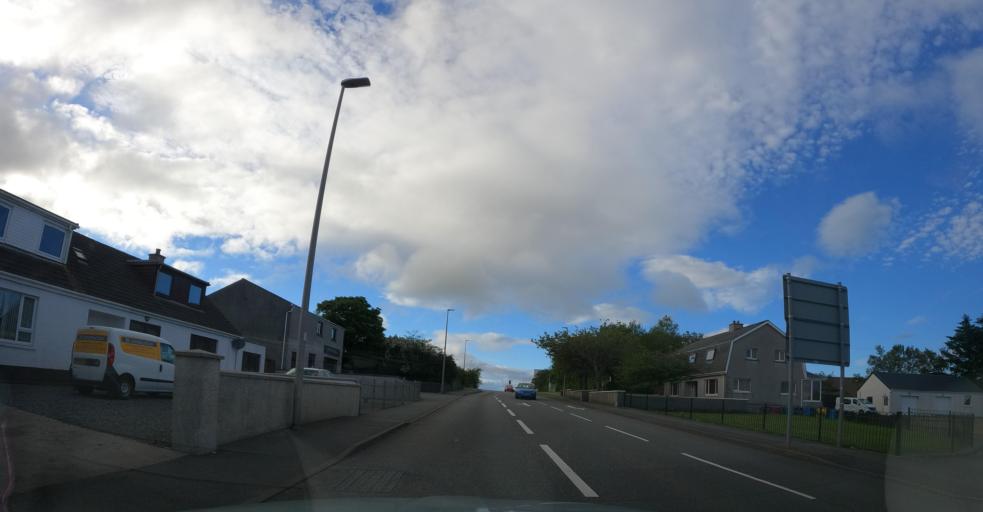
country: GB
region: Scotland
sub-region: Eilean Siar
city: Isle of Lewis
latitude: 58.2200
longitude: -6.3863
